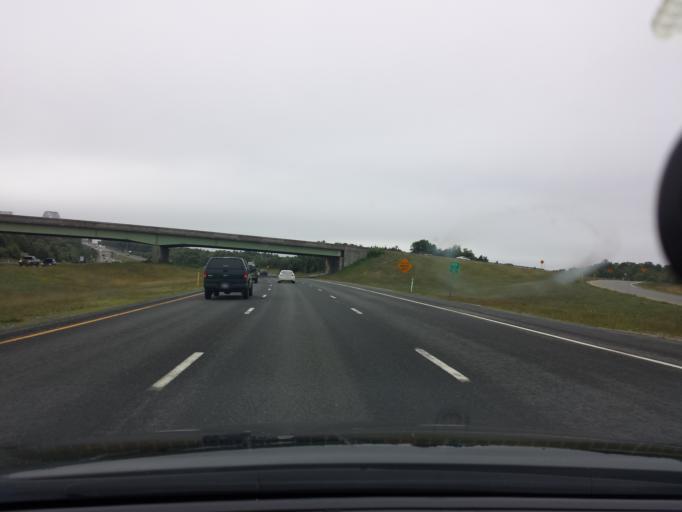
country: US
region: Massachusetts
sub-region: Barnstable County
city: Bourne
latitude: 41.7578
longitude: -70.5945
